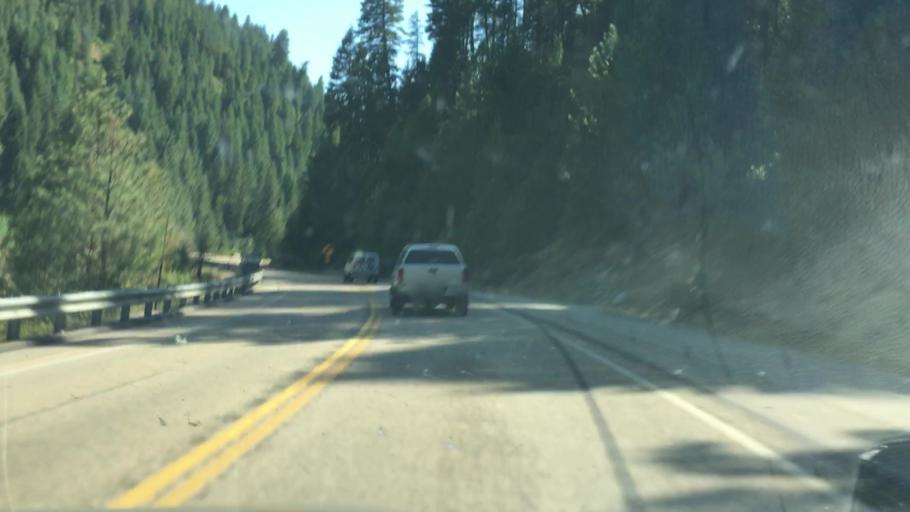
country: US
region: Idaho
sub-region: Valley County
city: Cascade
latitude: 44.1468
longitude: -116.1134
